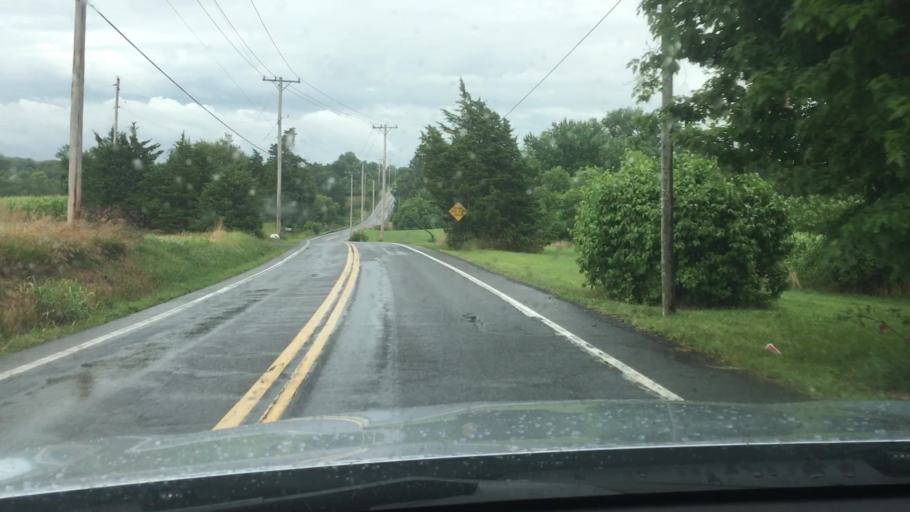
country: US
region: Pennsylvania
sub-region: Franklin County
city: Greencastle
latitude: 39.8633
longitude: -77.7489
